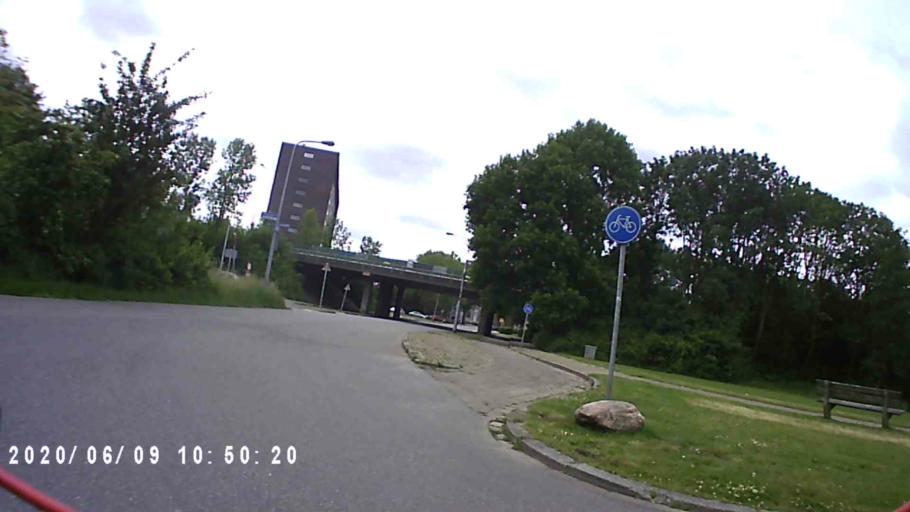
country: NL
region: Groningen
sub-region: Gemeente Groningen
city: Korrewegwijk
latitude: 53.2389
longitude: 6.5544
